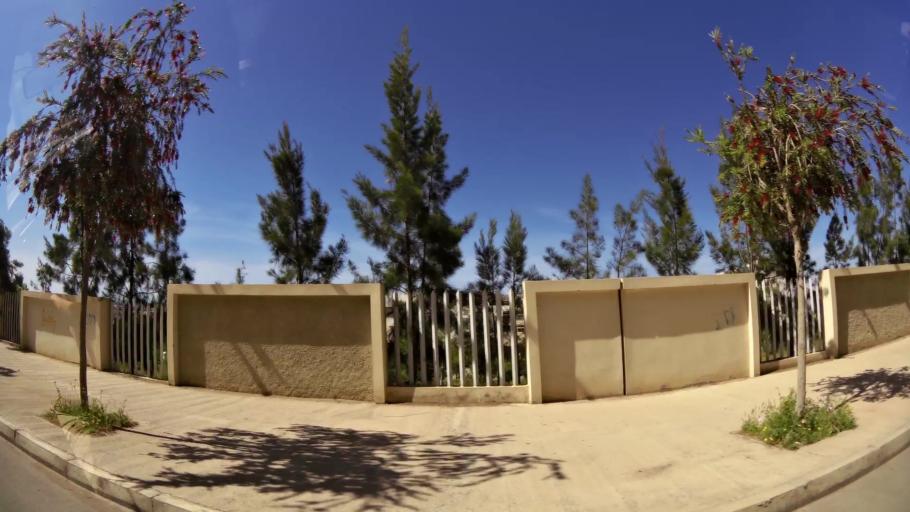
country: MA
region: Oriental
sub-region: Oujda-Angad
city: Oujda
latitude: 34.6550
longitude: -1.9110
